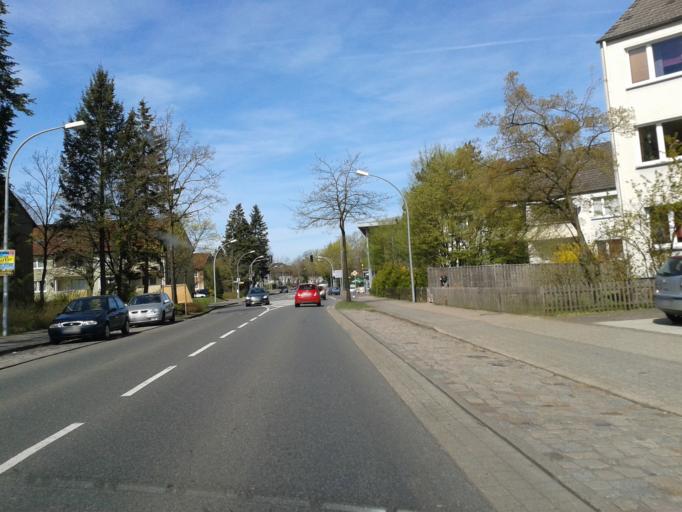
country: DE
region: Lower Saxony
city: Munster
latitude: 52.9861
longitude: 10.0863
